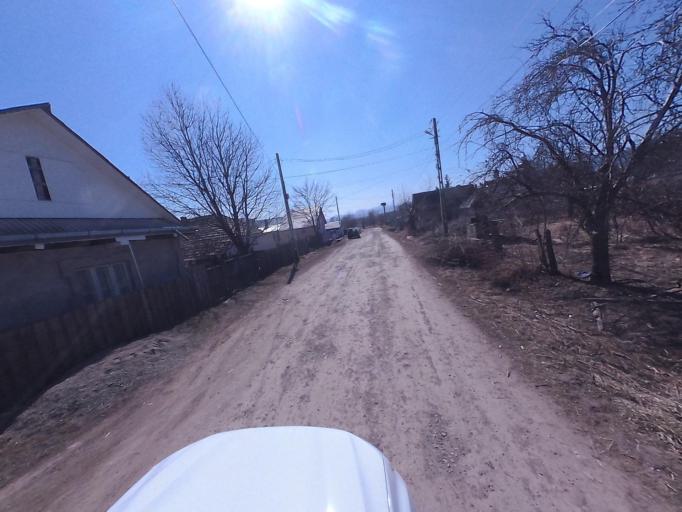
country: RO
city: Vanatori-Neamt
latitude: 47.1834
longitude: 26.3293
